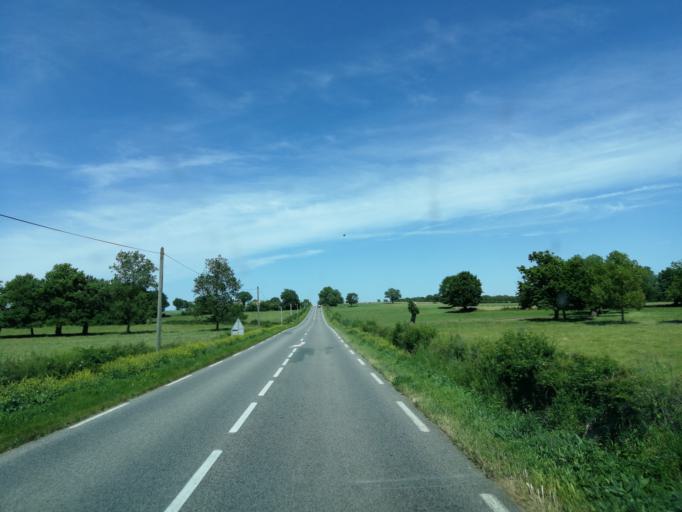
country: FR
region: Poitou-Charentes
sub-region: Departement des Deux-Sevres
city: Saint-Varent
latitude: 46.8830
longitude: -0.3190
